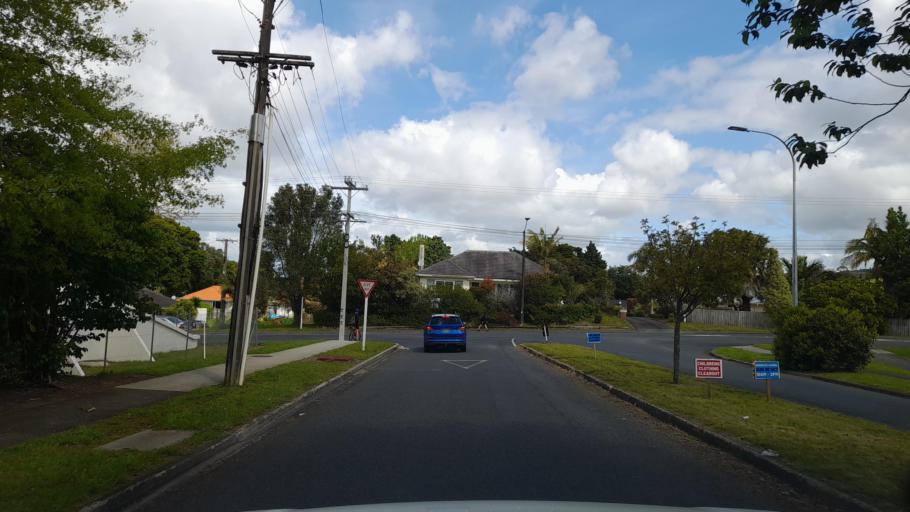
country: NZ
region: Northland
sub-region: Whangarei
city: Whangarei
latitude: -35.6967
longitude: 174.3052
